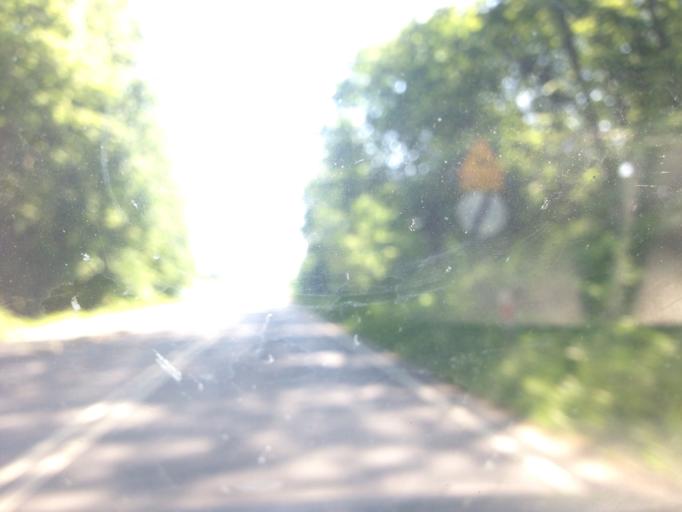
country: PL
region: Pomeranian Voivodeship
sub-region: Powiat tczewski
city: Pelplin
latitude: 53.9262
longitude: 18.6591
